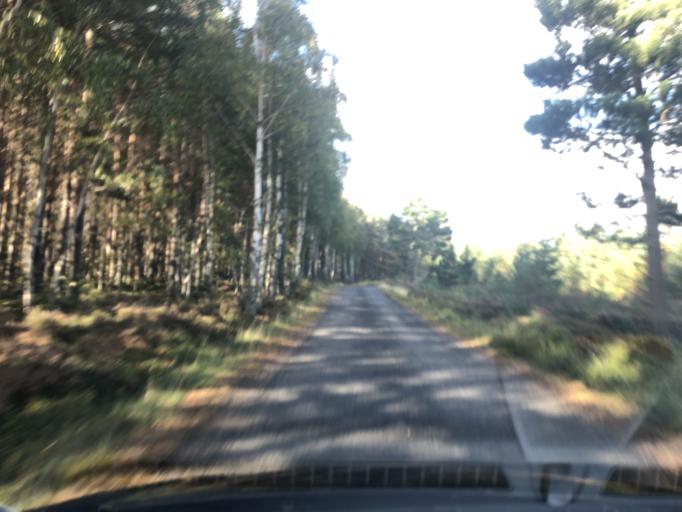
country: GB
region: Scotland
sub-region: Highland
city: Aviemore
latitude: 57.0688
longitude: -3.9016
